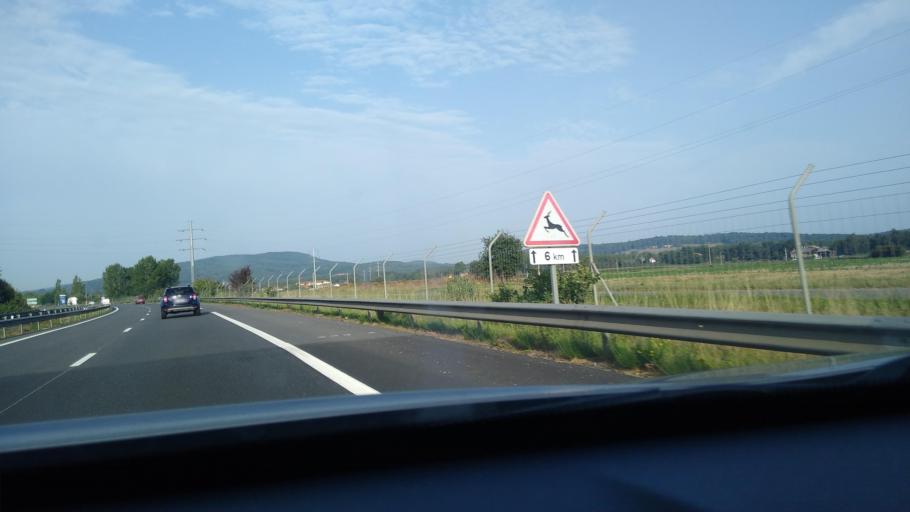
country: FR
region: Midi-Pyrenees
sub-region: Departement de la Haute-Garonne
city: Martres-Tolosane
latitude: 43.2073
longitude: 1.0196
